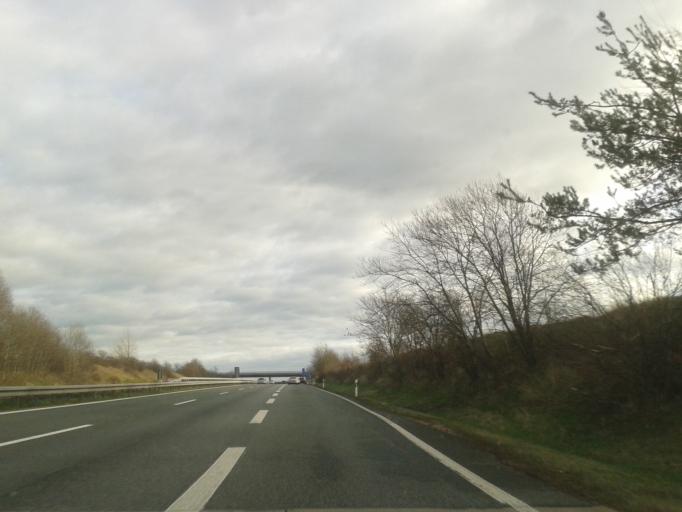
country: DE
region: Saxony
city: Weissenberg
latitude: 51.2063
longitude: 14.6584
